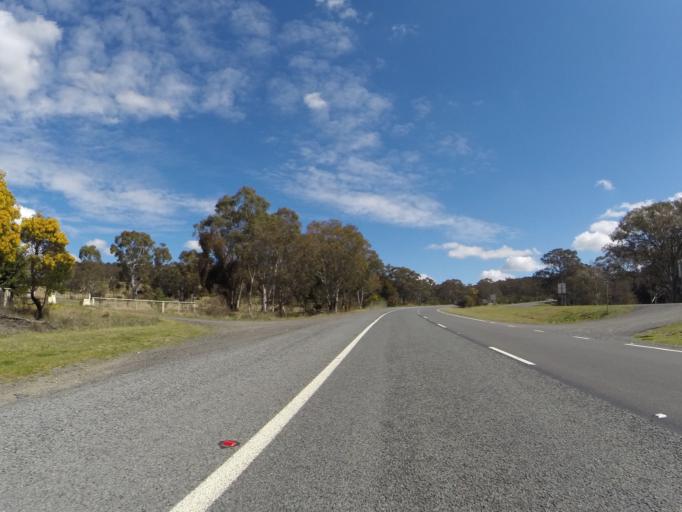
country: AU
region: New South Wales
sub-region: Goulburn Mulwaree
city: Goulburn
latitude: -34.7425
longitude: 149.7679
